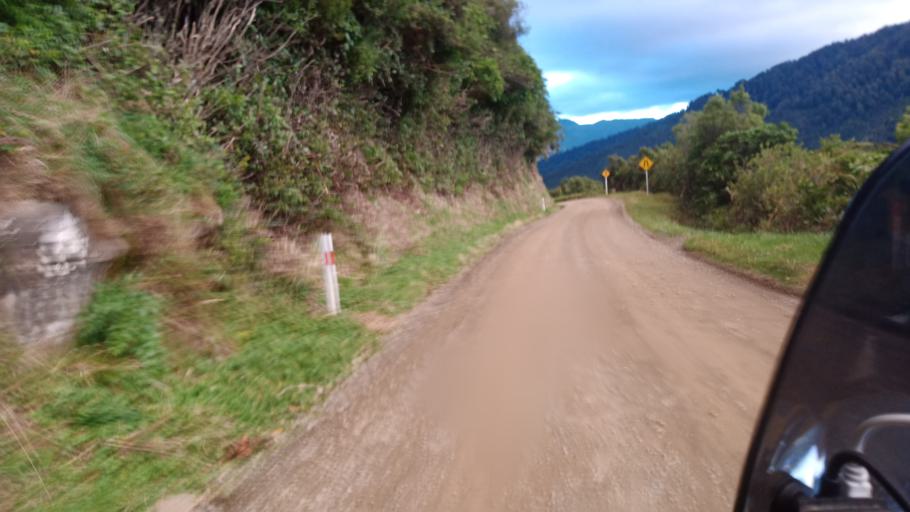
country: NZ
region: Hawke's Bay
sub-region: Wairoa District
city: Wairoa
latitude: -38.7271
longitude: 177.0657
